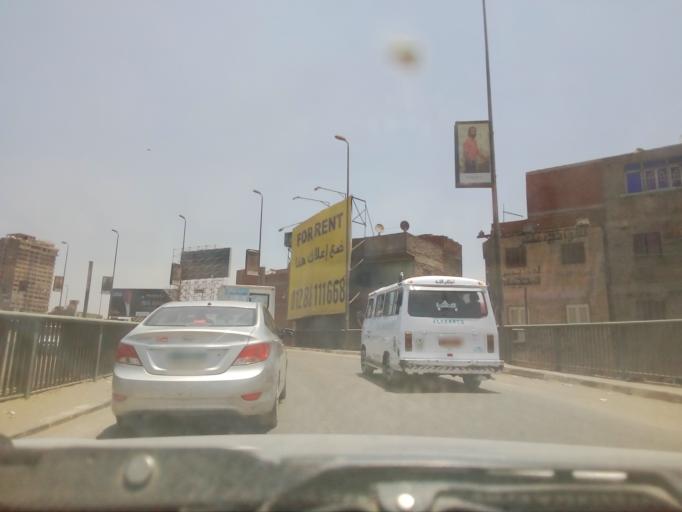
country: EG
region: Al Jizah
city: Al Jizah
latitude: 29.9853
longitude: 31.2147
